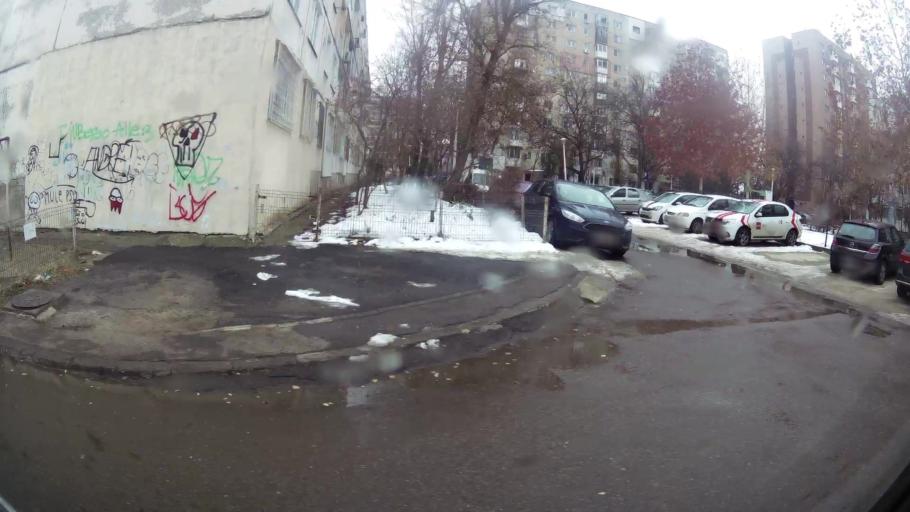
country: RO
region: Ilfov
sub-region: Comuna Chiajna
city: Rosu
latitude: 44.4238
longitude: 26.0135
